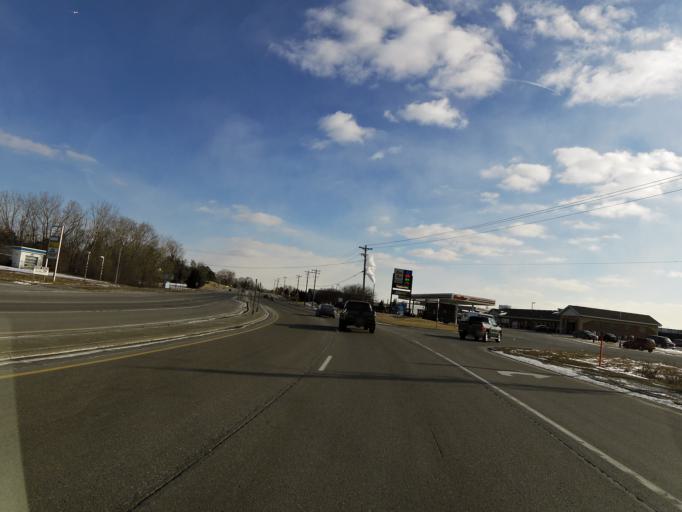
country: US
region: Minnesota
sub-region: Dakota County
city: Mendota Heights
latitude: 44.8450
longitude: -93.1239
